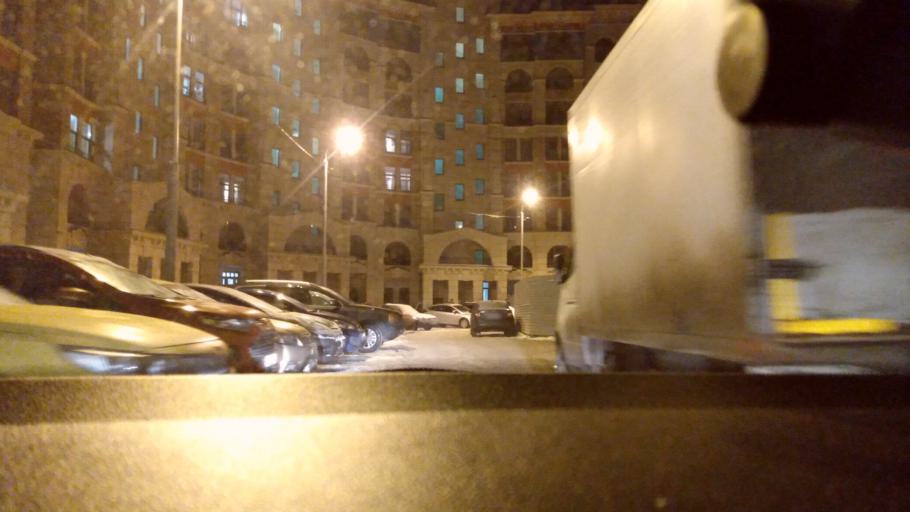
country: RU
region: Moskovskaya
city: Opalikha
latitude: 55.8166
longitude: 37.2468
